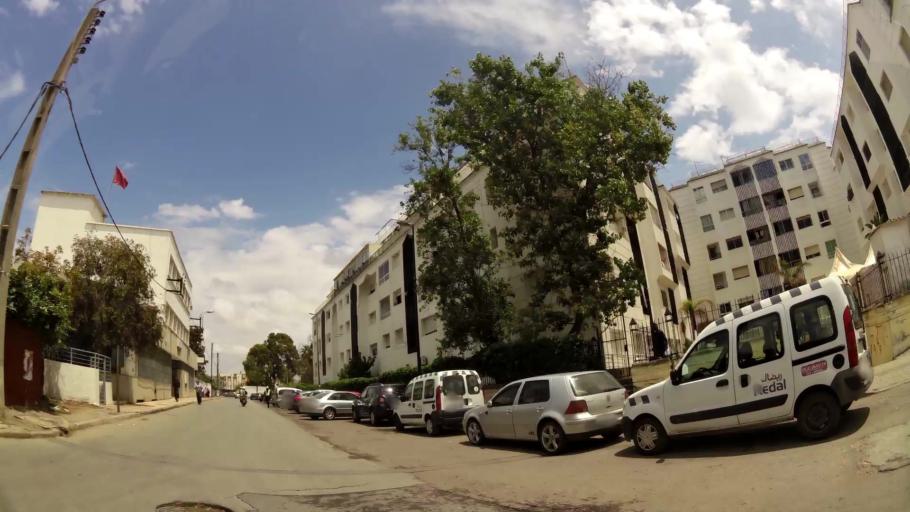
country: MA
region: Rabat-Sale-Zemmour-Zaer
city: Sale
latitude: 34.0432
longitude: -6.8187
